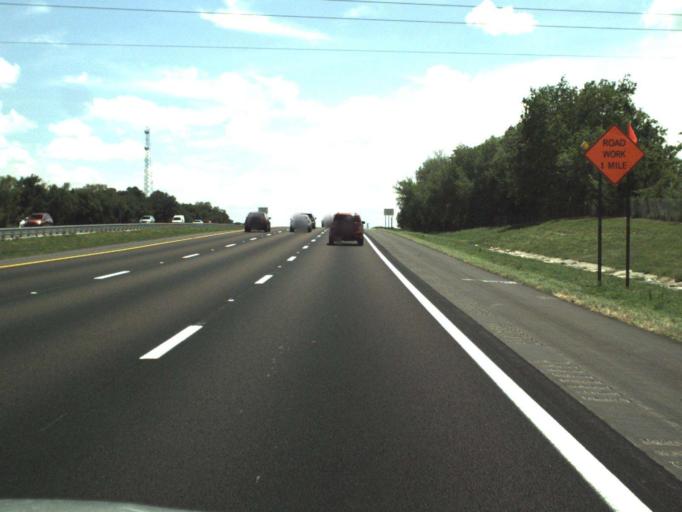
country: US
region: Florida
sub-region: Seminole County
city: Heathrow
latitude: 28.7322
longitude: -81.3720
